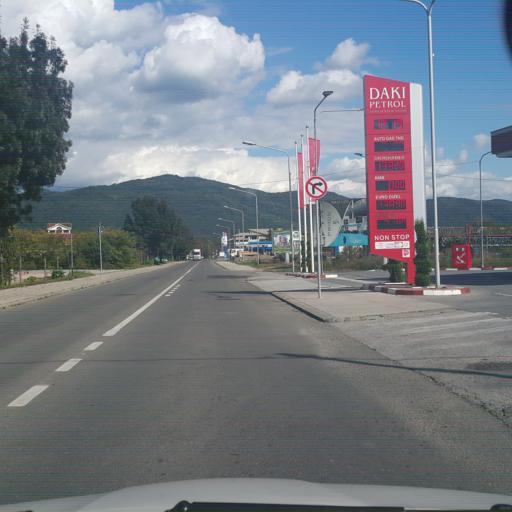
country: RS
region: Central Serbia
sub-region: Raski Okrug
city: Vrnjacka Banja
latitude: 43.6371
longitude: 20.9156
